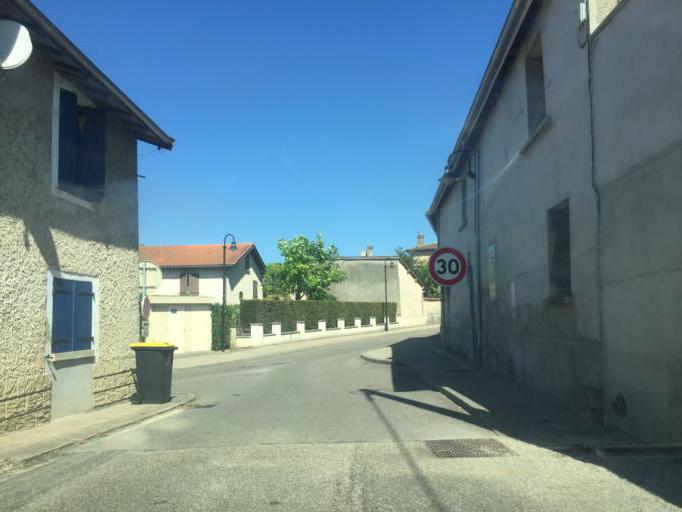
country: FR
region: Rhone-Alpes
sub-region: Departement de l'Ain
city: Tramoyes
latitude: 45.8765
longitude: 4.9682
